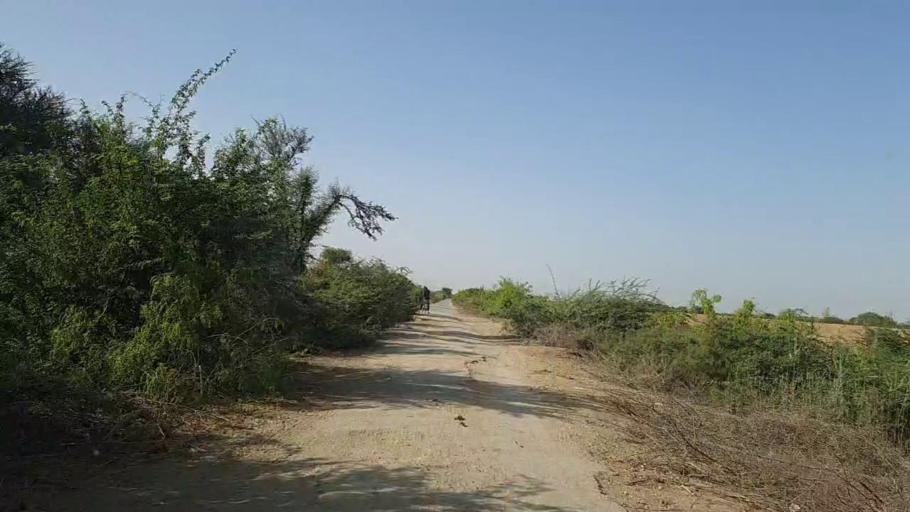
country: PK
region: Sindh
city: Kotri
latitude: 25.1540
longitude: 68.2646
